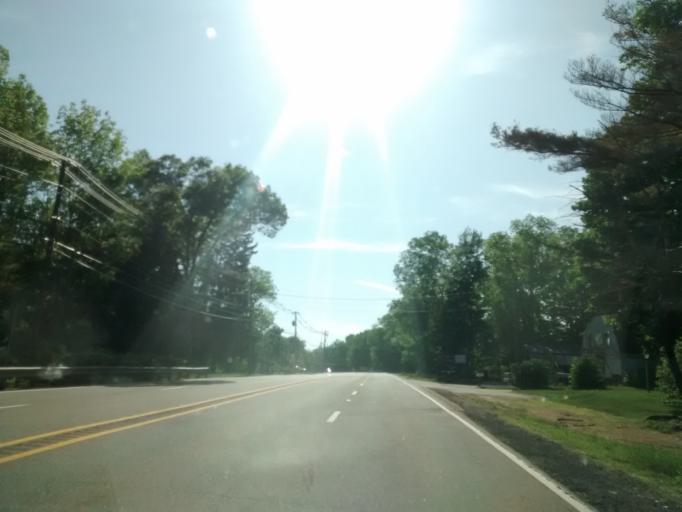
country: US
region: Massachusetts
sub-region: Worcester County
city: Charlton
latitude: 42.1386
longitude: -72.0222
